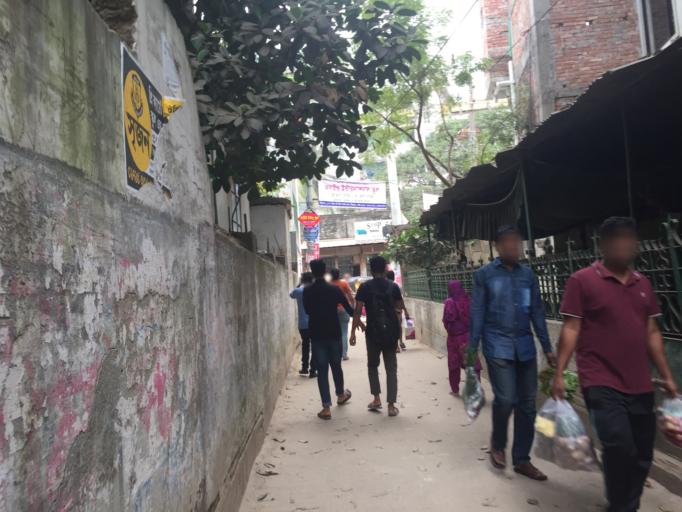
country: BD
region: Dhaka
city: Azimpur
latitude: 23.7910
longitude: 90.3567
